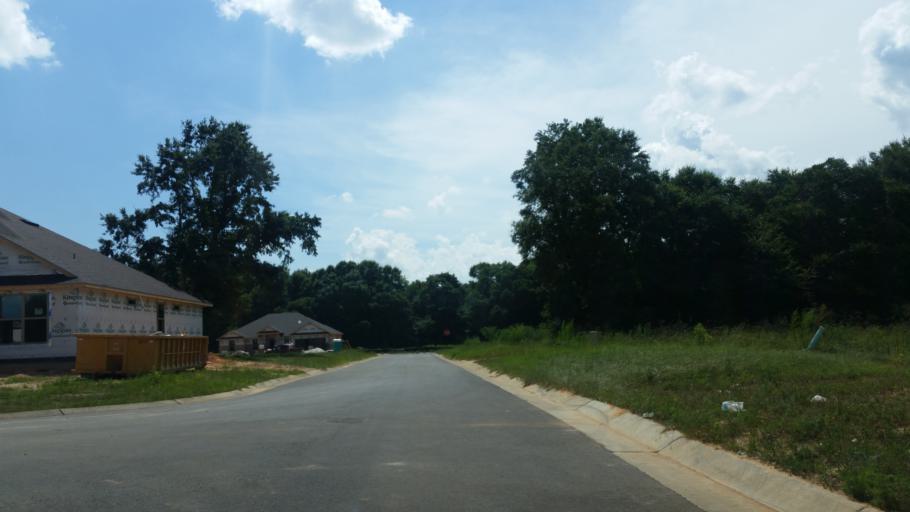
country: US
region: Florida
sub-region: Escambia County
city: Cantonment
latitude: 30.5542
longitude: -87.3699
